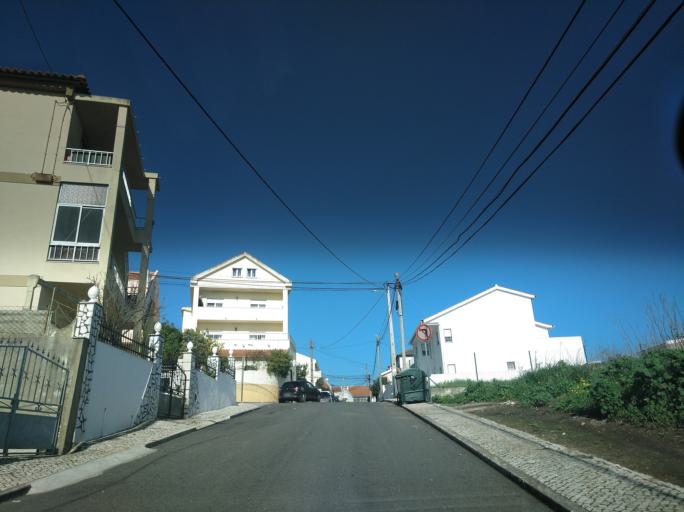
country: PT
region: Lisbon
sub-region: Odivelas
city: Famoes
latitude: 38.7919
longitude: -9.2190
